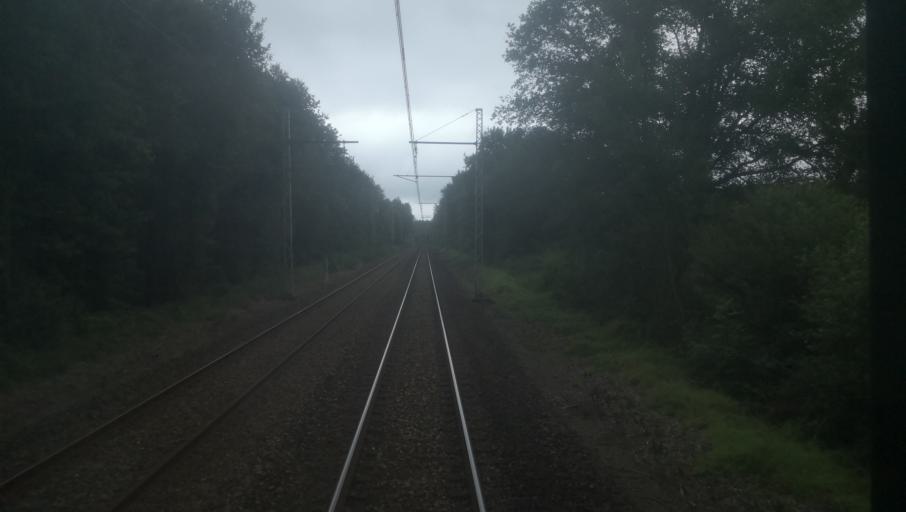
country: FR
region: Centre
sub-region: Departement de l'Indre
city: Luant
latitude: 46.7221
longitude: 1.5818
